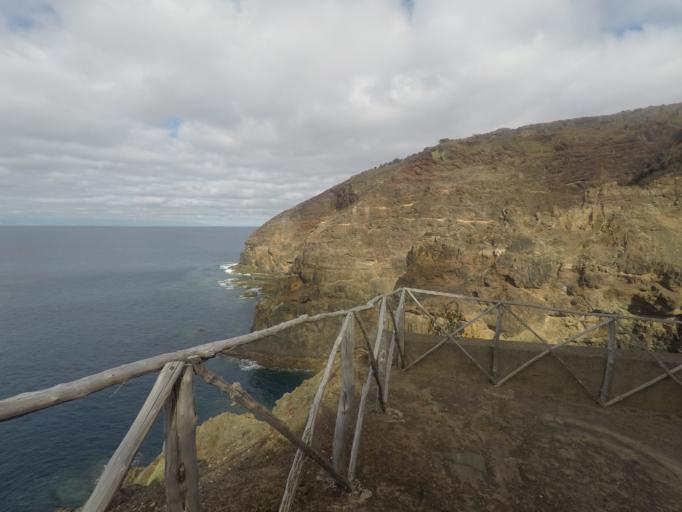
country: PT
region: Madeira
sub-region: Porto Santo
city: Vila de Porto Santo
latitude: 33.0318
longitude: -16.3873
